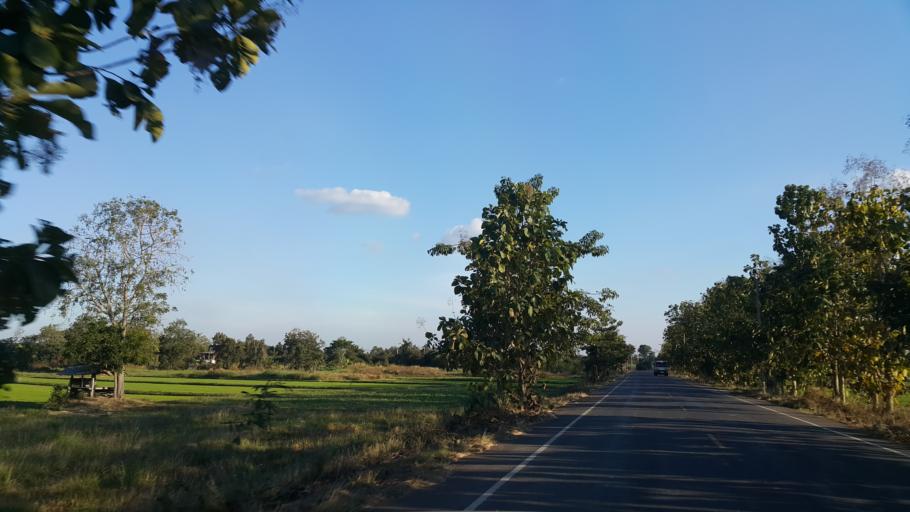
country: TH
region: Sukhothai
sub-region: Amphoe Si Satchanalai
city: Si Satchanalai
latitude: 17.5390
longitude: 99.7986
